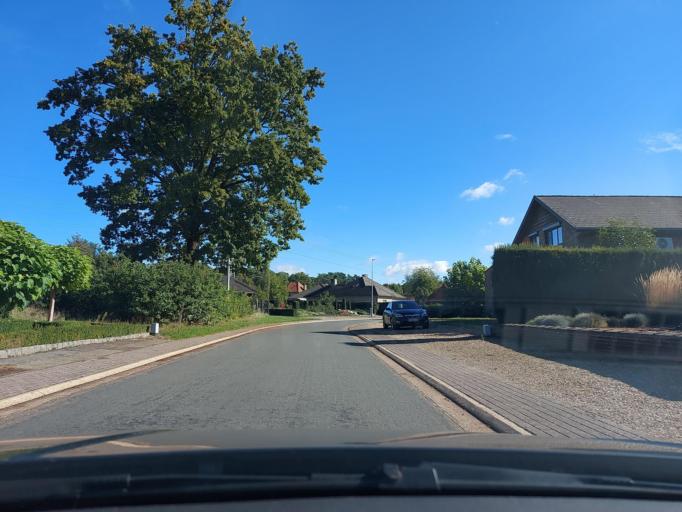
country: BE
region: Flanders
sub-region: Provincie Limburg
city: Houthalen
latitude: 51.0301
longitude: 5.3570
